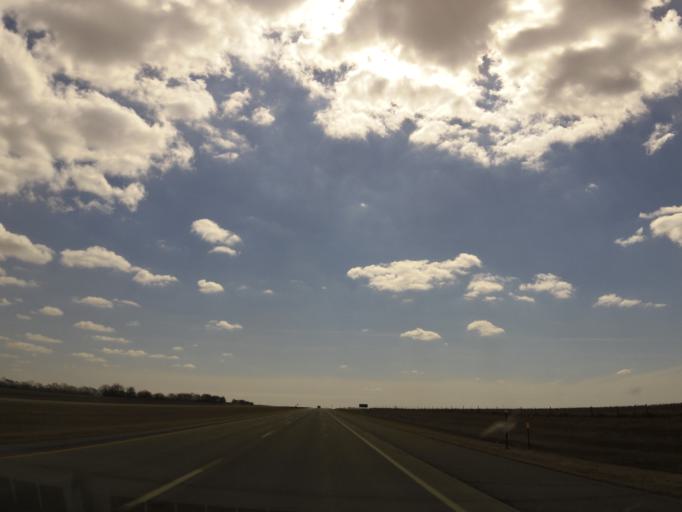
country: US
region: South Dakota
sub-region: Codington County
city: Watertown
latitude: 45.0676
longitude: -97.0559
